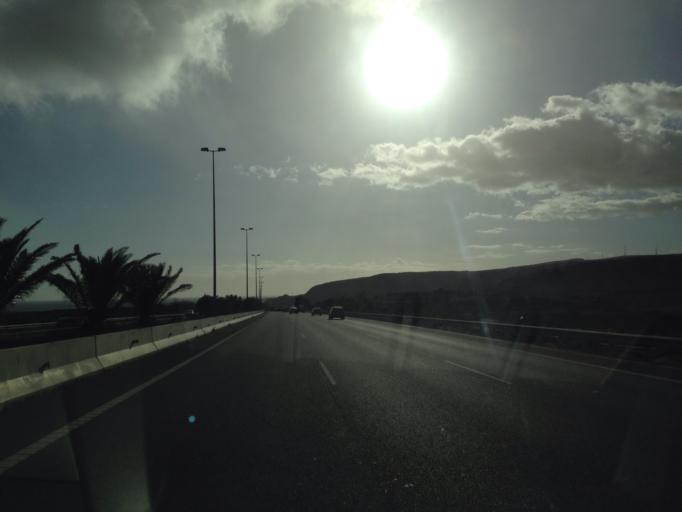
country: ES
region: Canary Islands
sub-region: Provincia de Las Palmas
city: Cruce de Arinaga
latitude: 27.8115
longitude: -15.4766
